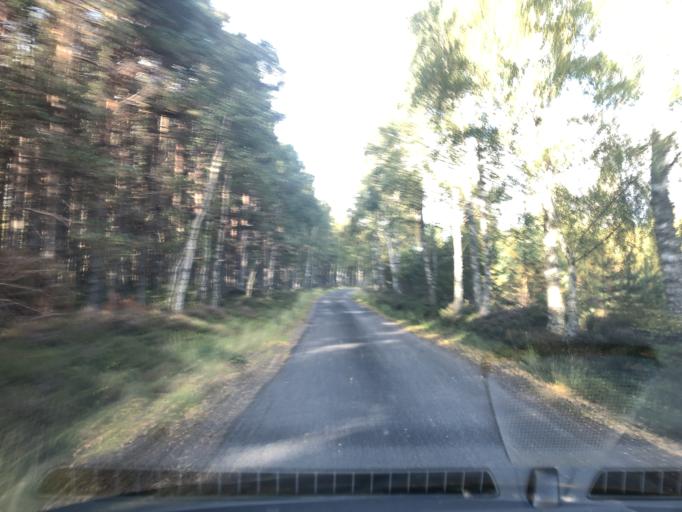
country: GB
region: Scotland
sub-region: Highland
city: Aviemore
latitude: 57.0699
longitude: -3.9021
